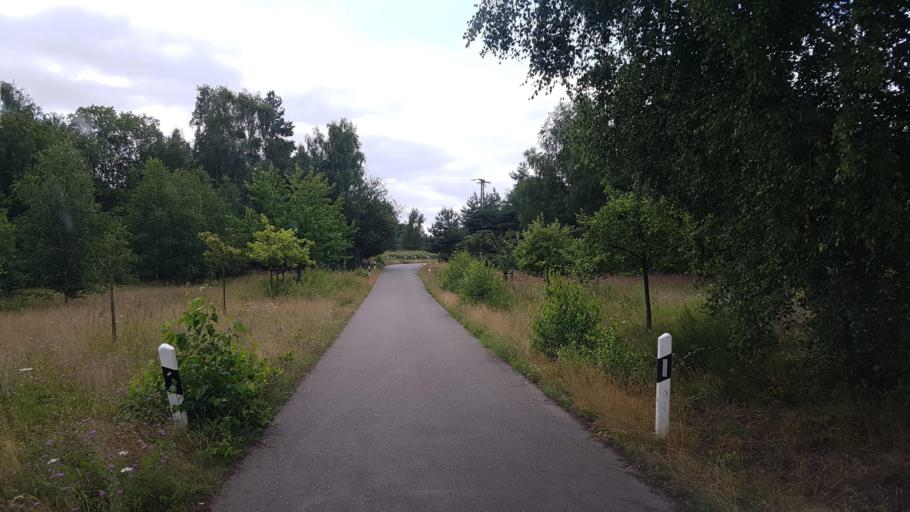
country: DE
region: Brandenburg
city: Altdobern
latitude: 51.6455
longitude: 14.0852
